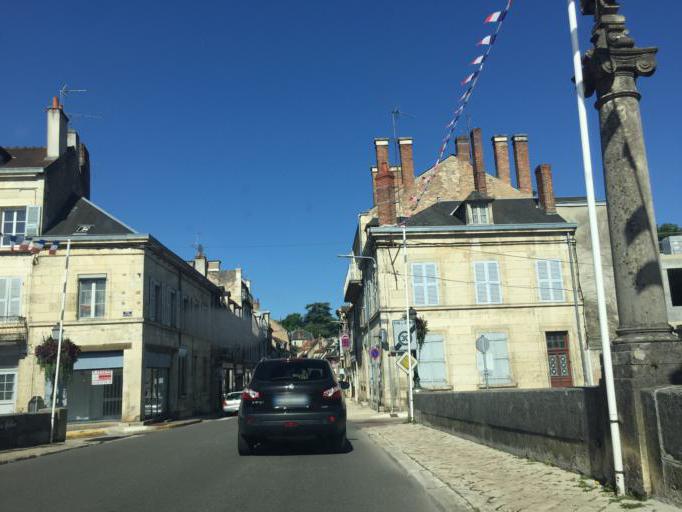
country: FR
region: Bourgogne
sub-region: Departement de la Nievre
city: Clamecy
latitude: 47.4600
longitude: 3.5175
